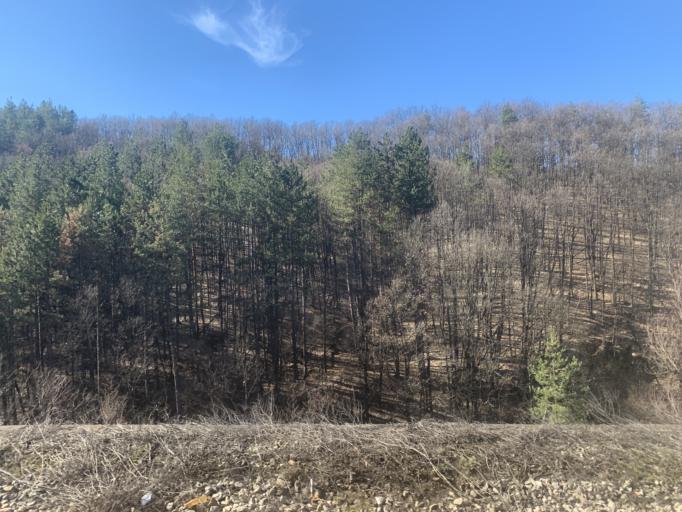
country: BG
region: Sofiya
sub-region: Obshtina Gorna Malina
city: Gorna Malina
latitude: 42.5697
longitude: 23.6719
